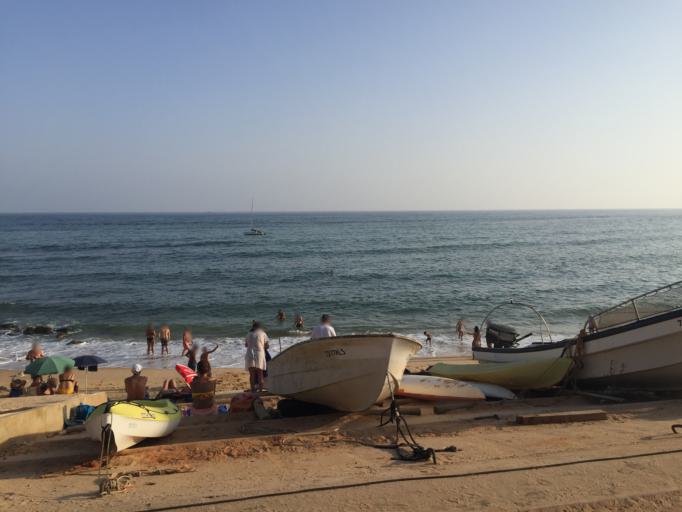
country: PT
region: Faro
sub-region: Loule
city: Boliqueime
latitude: 37.0900
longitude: -8.1891
